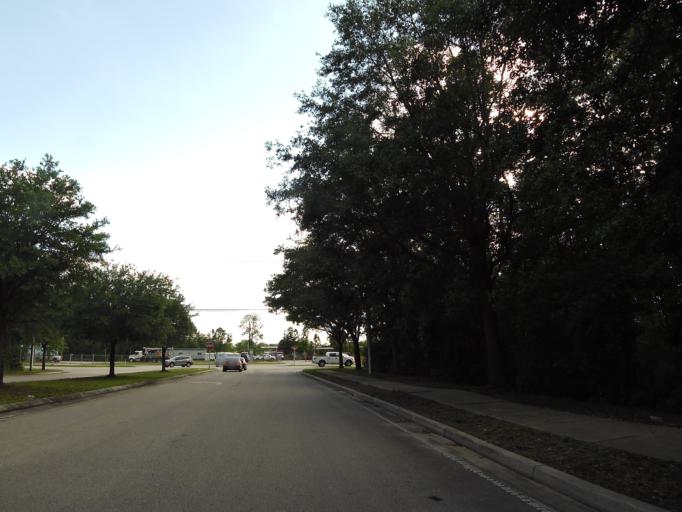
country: US
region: Florida
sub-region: Duval County
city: Jacksonville
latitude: 30.2419
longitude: -81.5973
